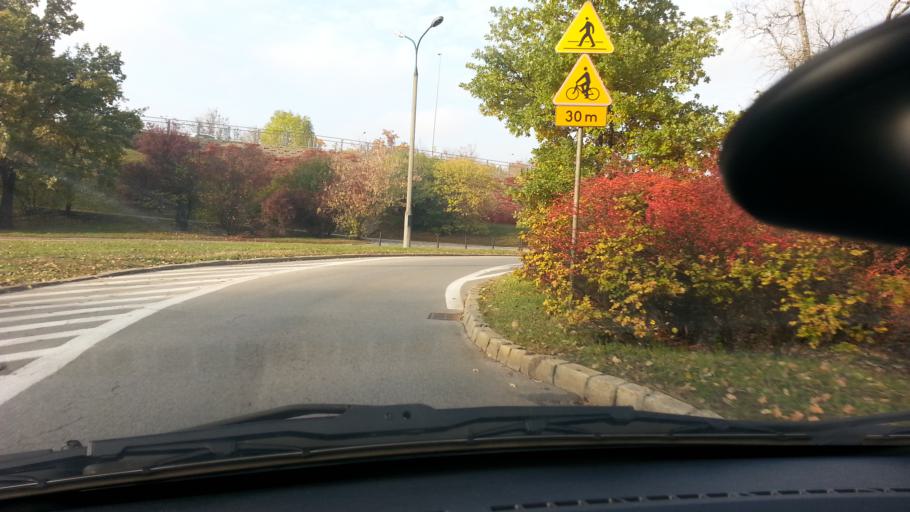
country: PL
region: Masovian Voivodeship
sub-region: Warszawa
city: Praga Polnoc
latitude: 52.2616
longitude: 21.0152
